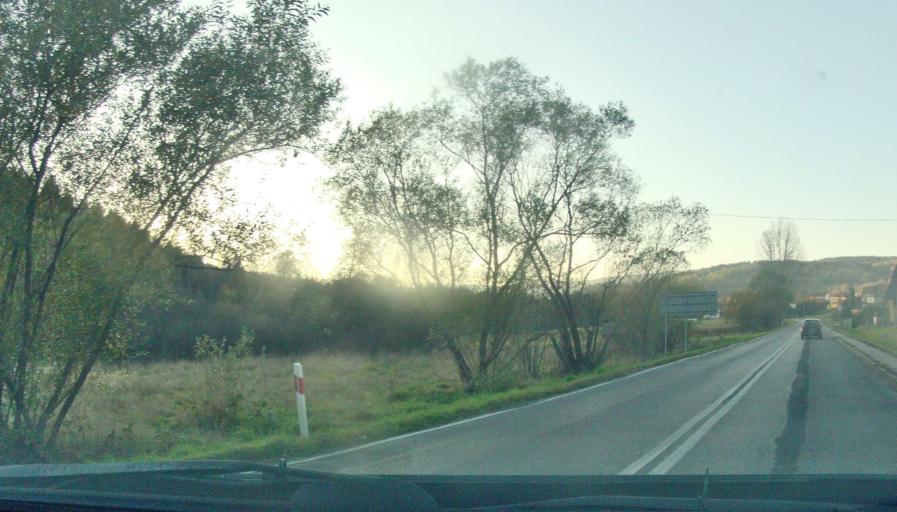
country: PL
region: Lesser Poland Voivodeship
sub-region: Powiat suski
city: Kukow
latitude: 49.7403
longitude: 19.4622
